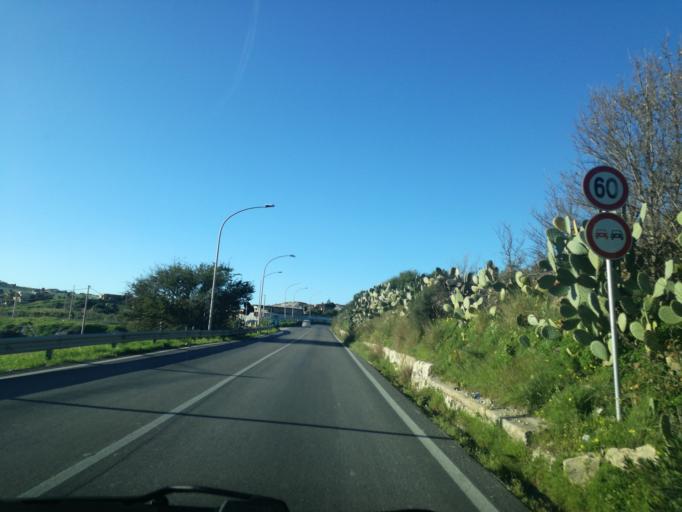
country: IT
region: Sicily
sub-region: Provincia di Caltanissetta
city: Gela
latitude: 37.1008
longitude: 14.1588
